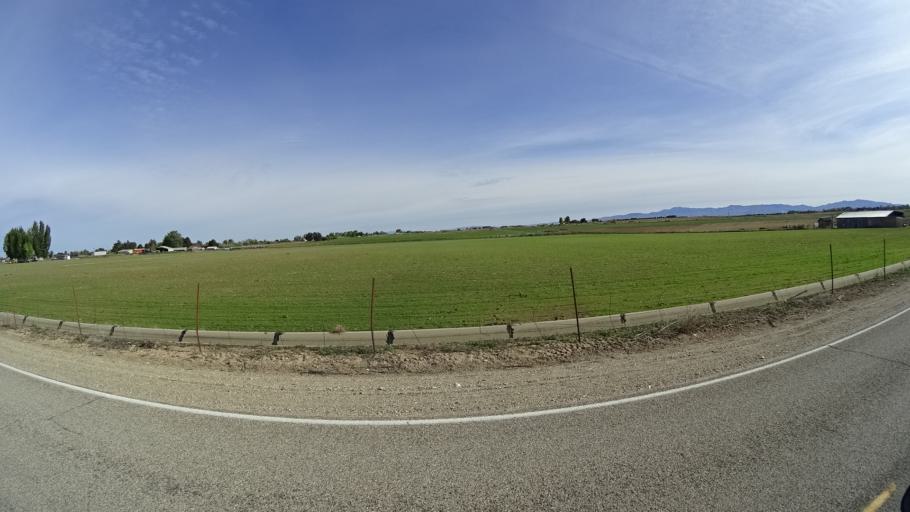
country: US
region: Idaho
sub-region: Ada County
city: Kuna
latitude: 43.4735
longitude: -116.3509
